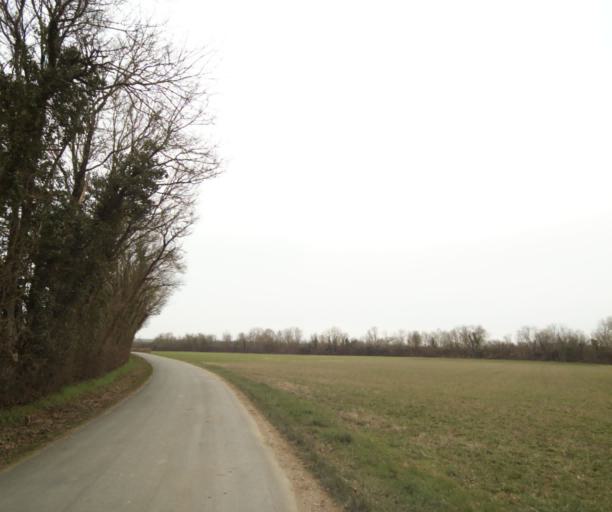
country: FR
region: Poitou-Charentes
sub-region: Departement des Deux-Sevres
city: Magne
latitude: 46.3284
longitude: -0.5281
